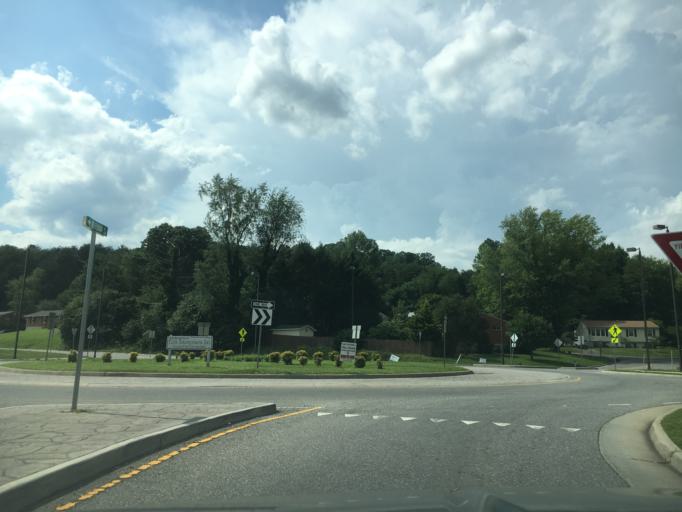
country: US
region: Virginia
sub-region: Roanoke County
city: Cave Spring
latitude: 37.2038
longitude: -80.0007
